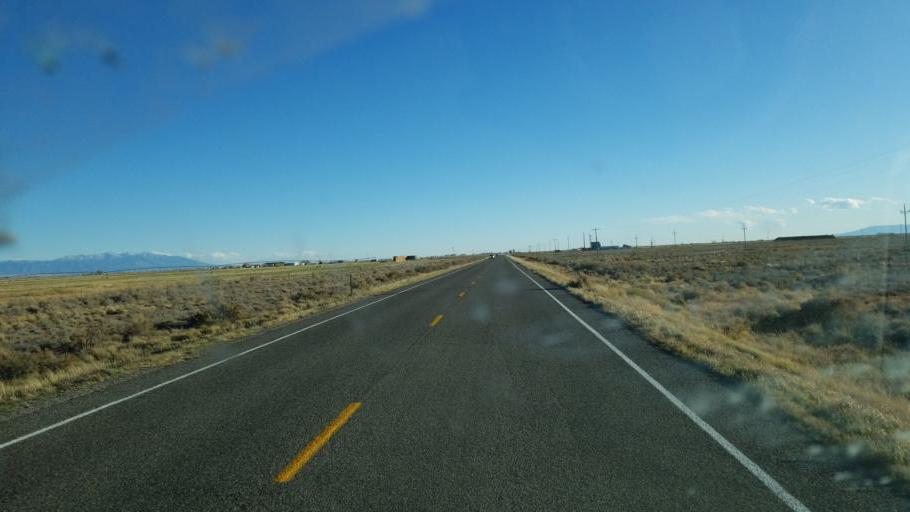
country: US
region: Colorado
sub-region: Saguache County
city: Saguache
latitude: 38.1075
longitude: -105.9205
